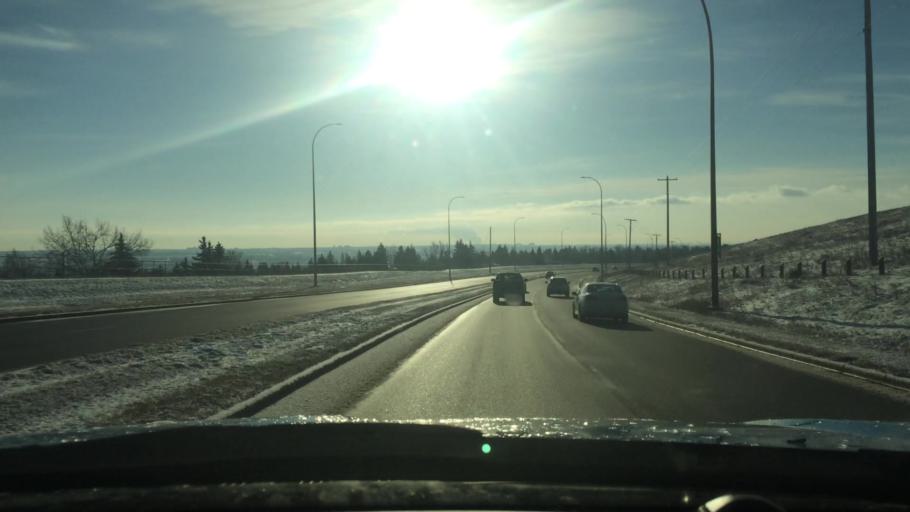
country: CA
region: Alberta
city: Calgary
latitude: 51.1177
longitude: -114.0870
